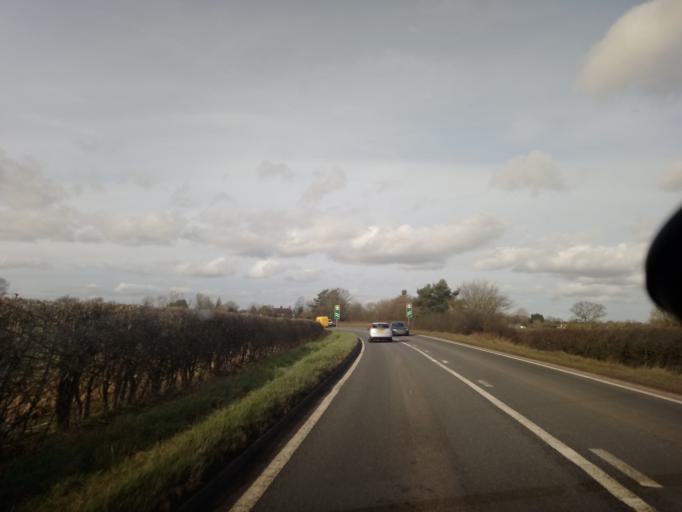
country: GB
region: England
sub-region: Telford and Wrekin
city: Eyton upon the Weald Moors
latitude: 52.7518
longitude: -2.5443
